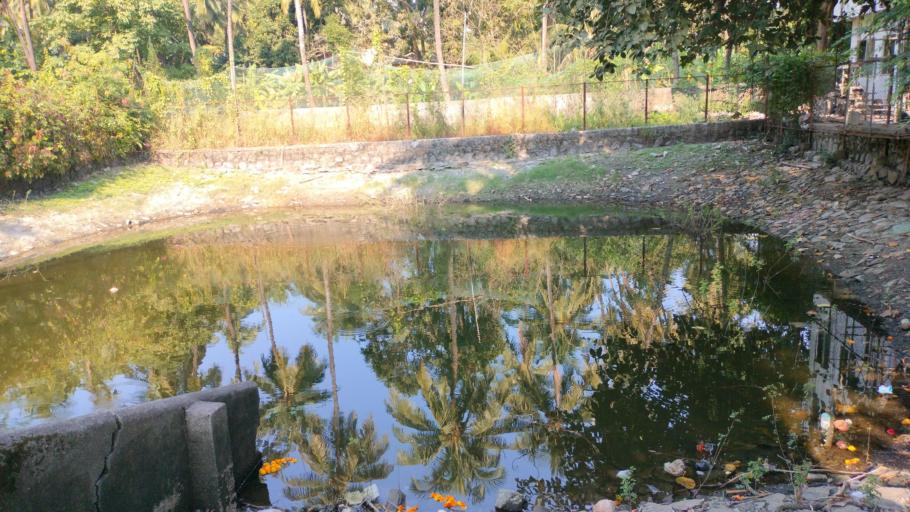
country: IN
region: Maharashtra
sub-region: Thane
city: Bhayandar
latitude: 19.3473
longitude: 72.7986
